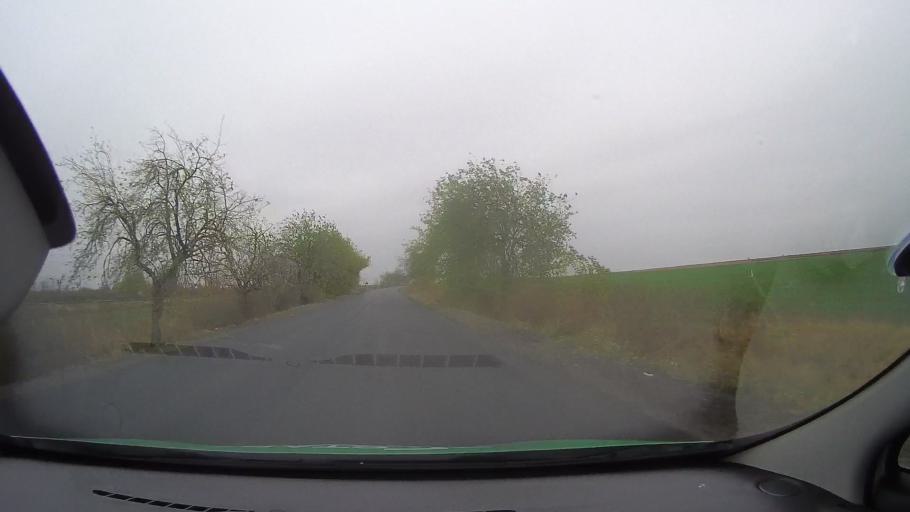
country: RO
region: Ialomita
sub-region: Comuna Valea Ciorii
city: Valea Ciorii
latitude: 44.6965
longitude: 27.6010
